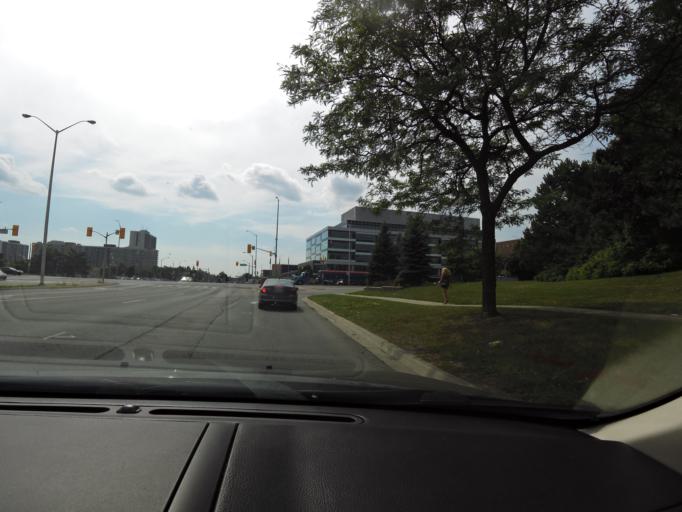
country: CA
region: Ontario
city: Brampton
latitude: 43.7207
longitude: -79.7225
